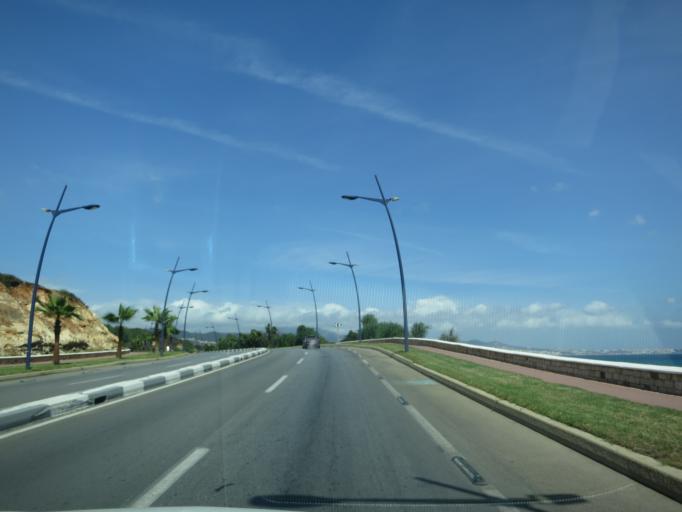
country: ES
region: Ceuta
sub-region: Ceuta
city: Ceuta
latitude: 35.7815
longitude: -5.3492
